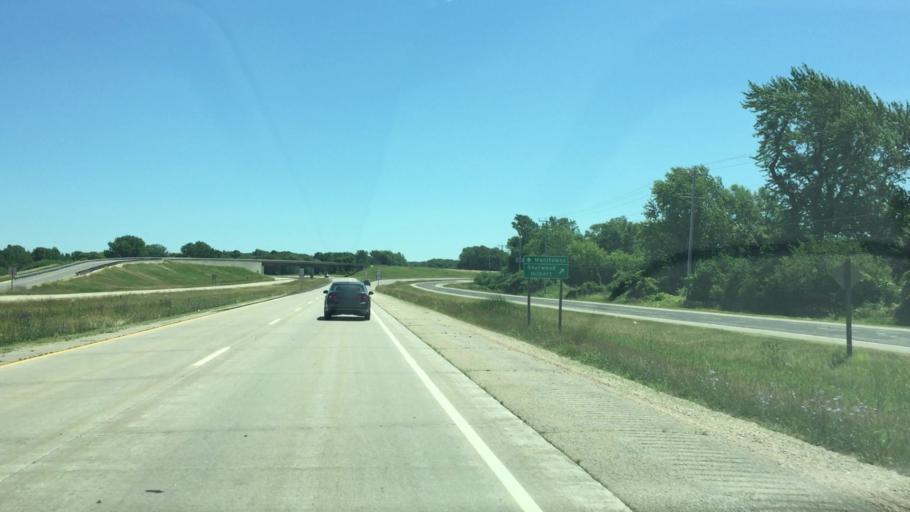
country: US
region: Wisconsin
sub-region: Outagamie County
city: Combined Locks
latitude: 44.2074
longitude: -88.3400
